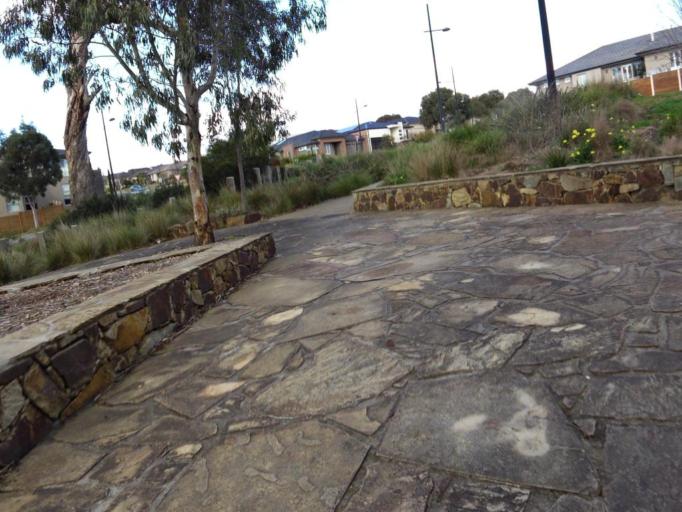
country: AU
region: Victoria
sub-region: Banyule
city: Watsonia North
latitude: -37.6857
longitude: 145.0796
